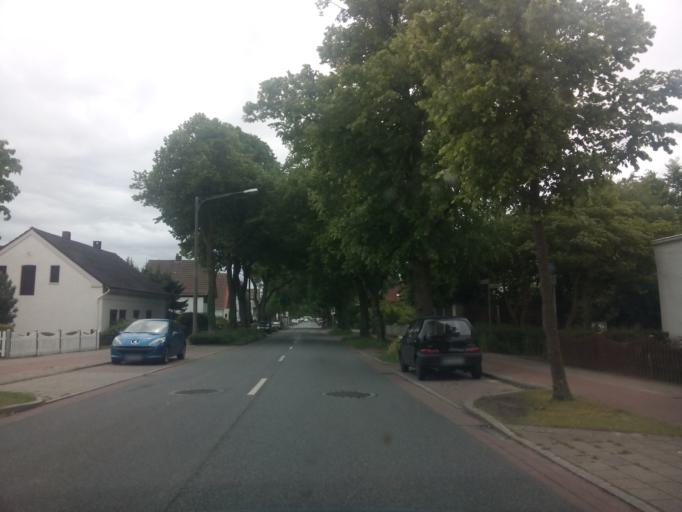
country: DE
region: Lower Saxony
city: Schwanewede
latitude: 53.2054
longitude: 8.5773
